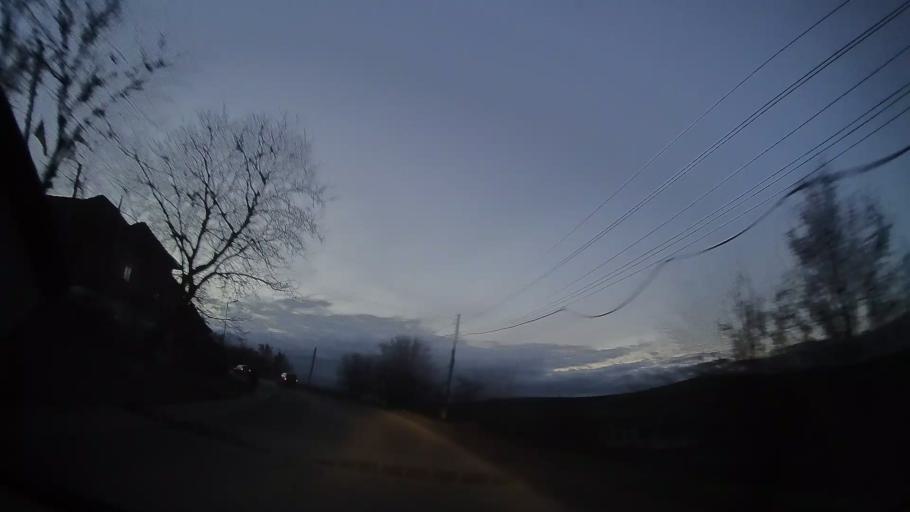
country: RO
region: Mures
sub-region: Comuna Sarmasu
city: Sarmasu
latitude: 46.7582
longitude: 24.1662
